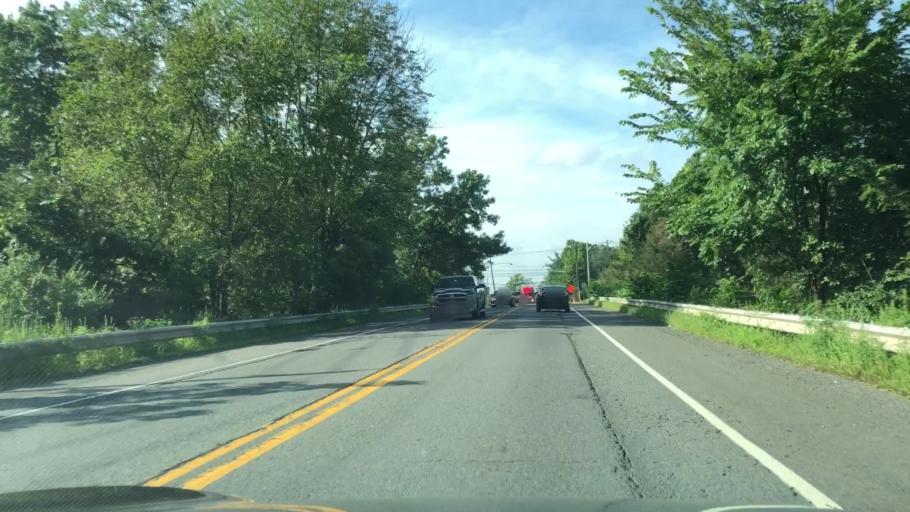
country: US
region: New Jersey
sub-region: Mercer County
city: Pennington
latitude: 40.3334
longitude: -74.7982
